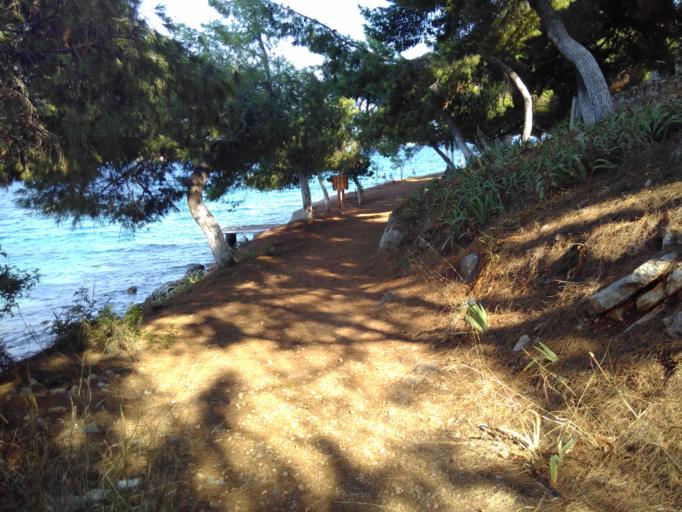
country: GR
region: West Greece
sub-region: Nomos Achaias
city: Selianitika
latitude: 38.3726
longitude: 22.0778
